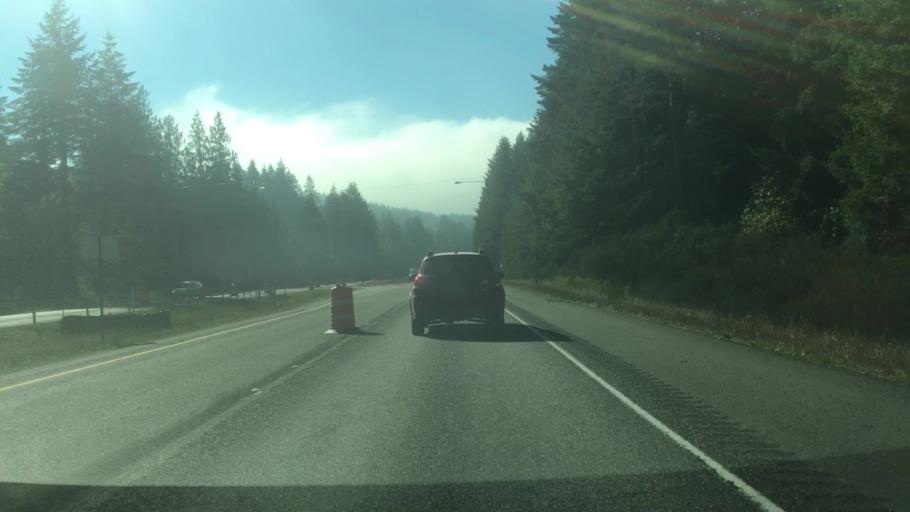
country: US
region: Washington
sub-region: Grays Harbor County
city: McCleary
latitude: 47.0448
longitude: -123.3150
